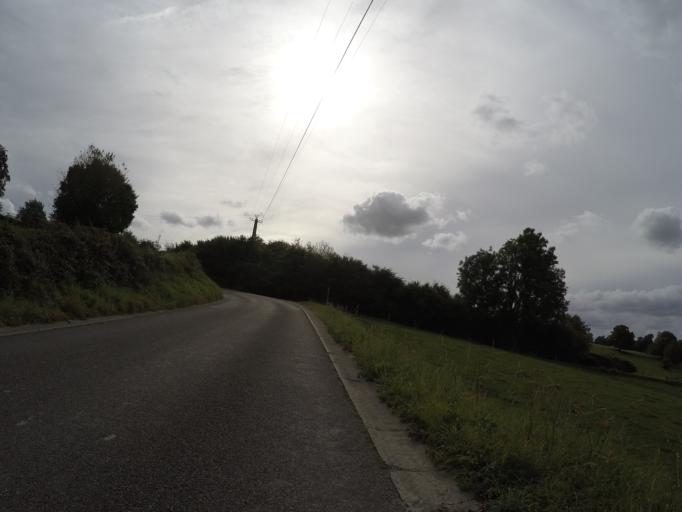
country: BE
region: Wallonia
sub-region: Province de Namur
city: Assesse
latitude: 50.3216
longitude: 4.9759
